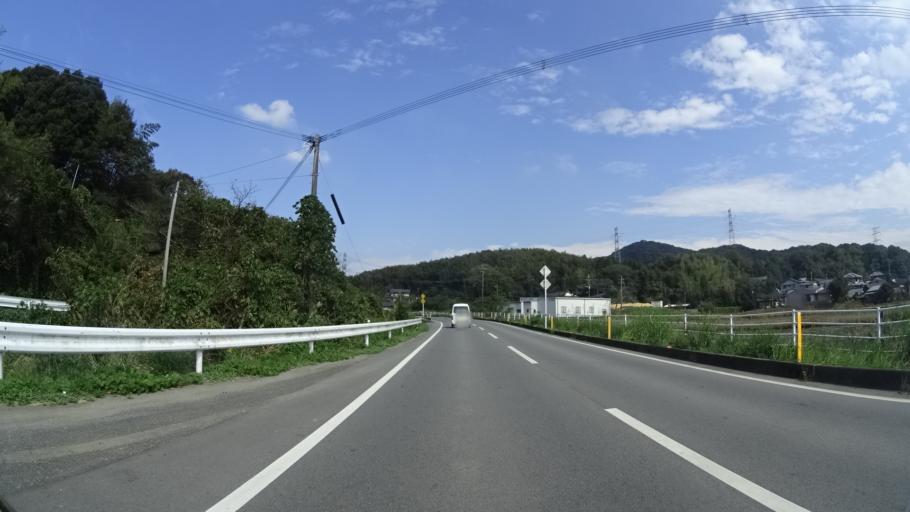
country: JP
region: Kumamoto
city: Matsubase
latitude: 32.6560
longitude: 130.7162
